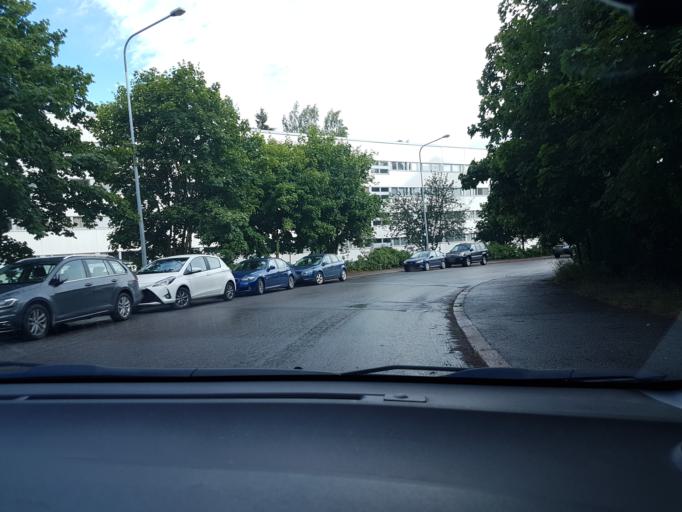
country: FI
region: Uusimaa
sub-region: Helsinki
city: Vantaa
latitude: 60.2355
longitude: 25.0022
